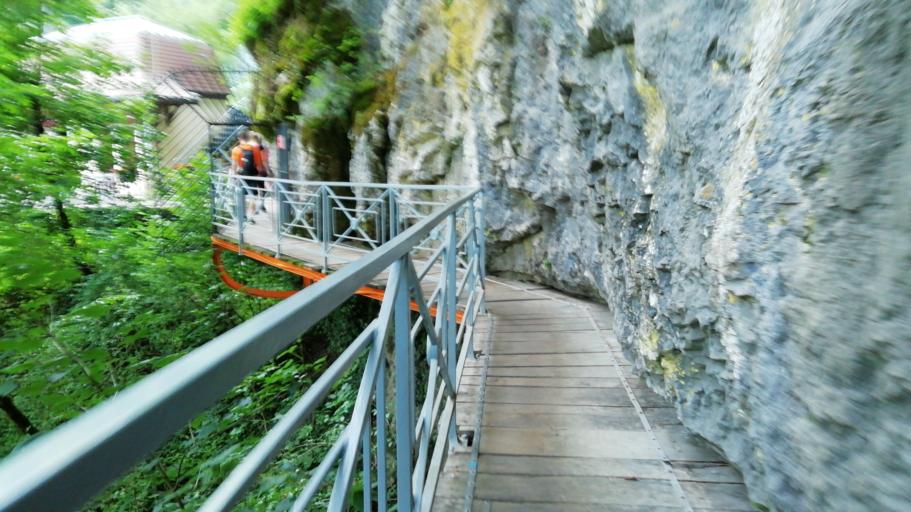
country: FR
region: Rhone-Alpes
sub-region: Departement de la Haute-Savoie
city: Chavanod
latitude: 45.8959
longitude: 6.0380
